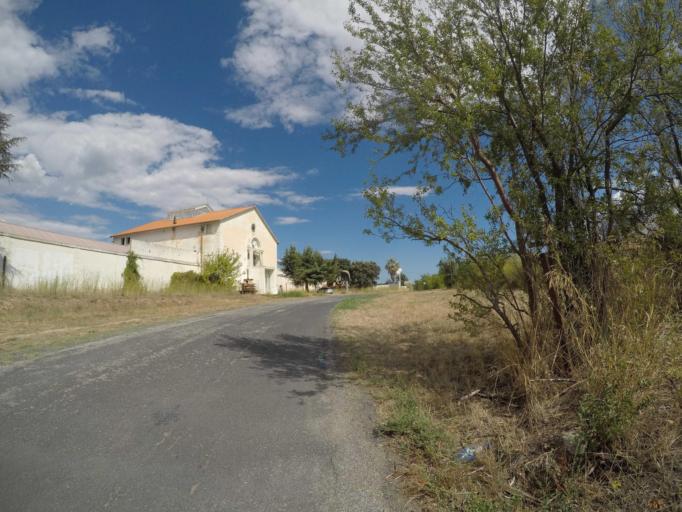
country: FR
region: Languedoc-Roussillon
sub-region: Departement des Pyrenees-Orientales
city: Ceret
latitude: 42.5050
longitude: 2.7642
